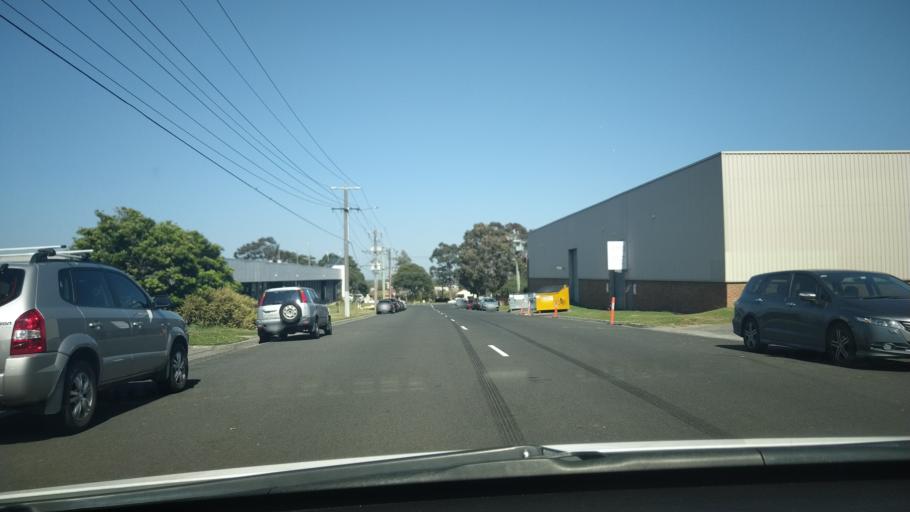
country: AU
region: Victoria
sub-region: Greater Dandenong
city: Noble Park North
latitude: -37.9561
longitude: 145.1850
